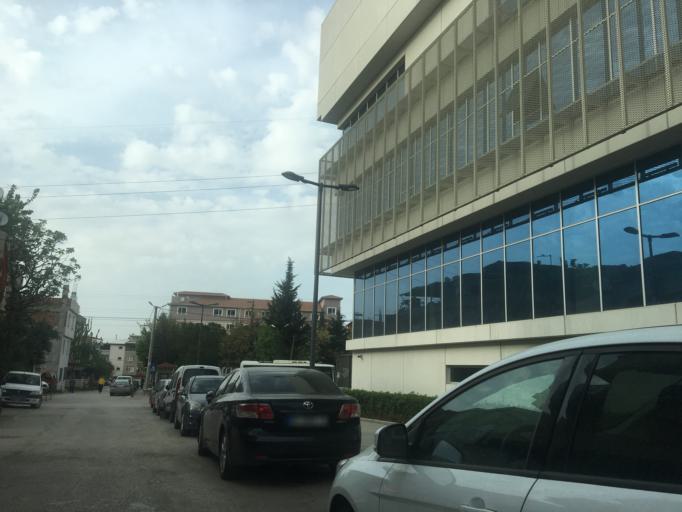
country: TR
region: Bursa
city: Yildirim
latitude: 40.2031
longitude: 29.0462
